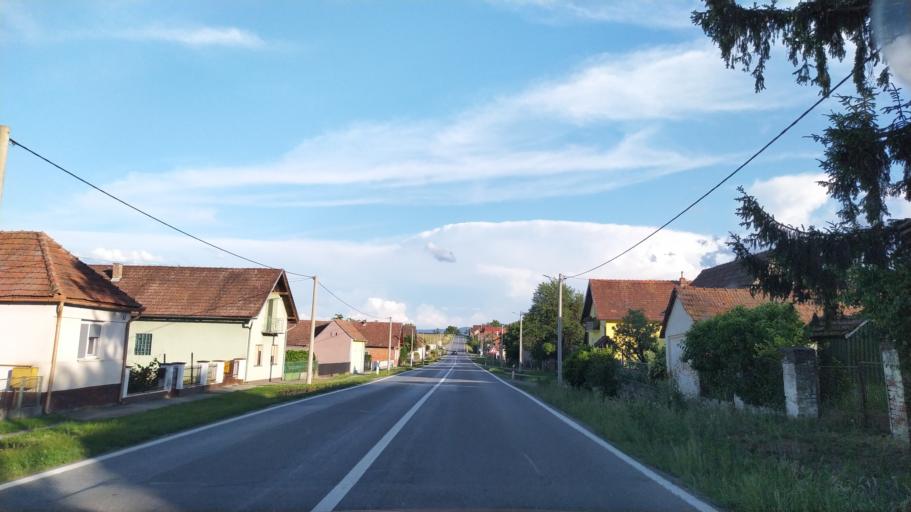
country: HR
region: Virovitick-Podravska
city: Slatina
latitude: 45.6585
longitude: 17.7739
